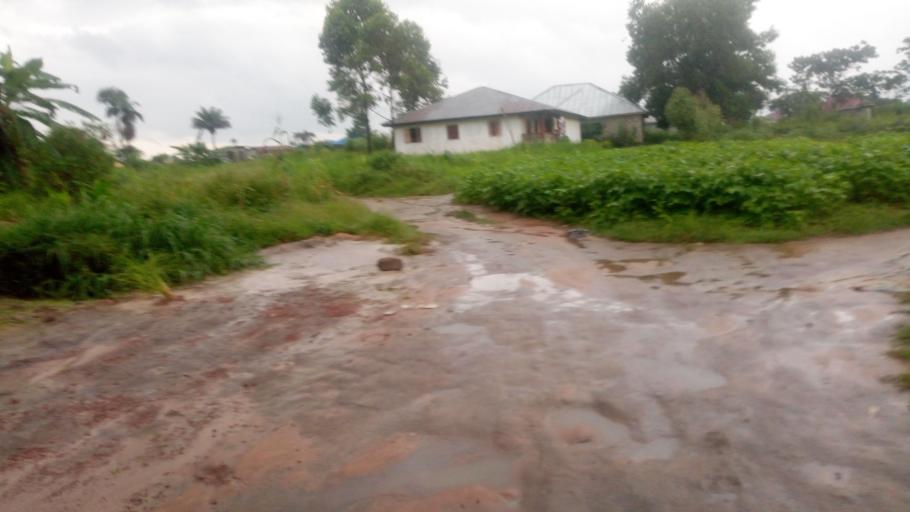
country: SL
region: Northern Province
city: Yonibana
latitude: 8.4685
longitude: -12.2346
